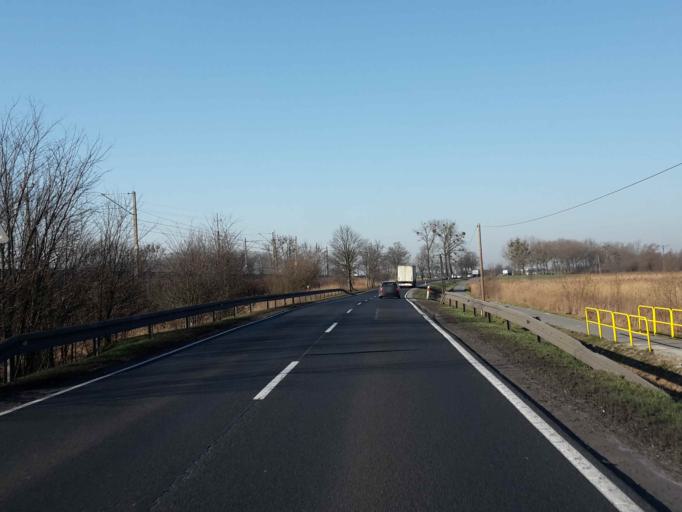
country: PL
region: Kujawsko-Pomorskie
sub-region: Powiat inowroclawski
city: Gniewkowo
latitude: 52.9048
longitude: 18.4624
